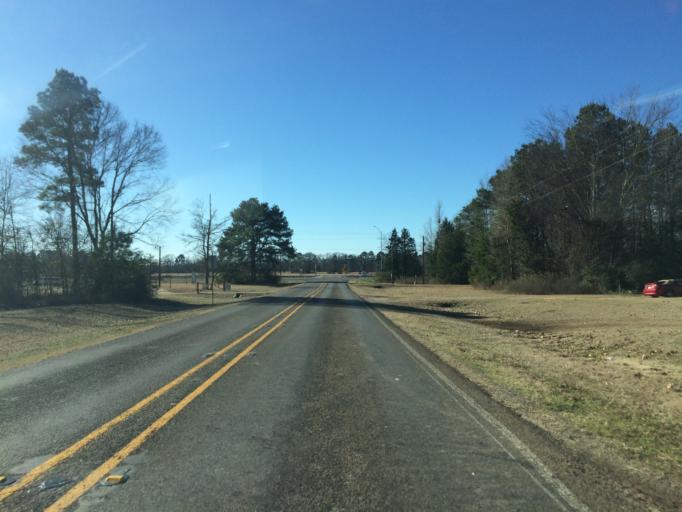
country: US
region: Texas
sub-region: Wood County
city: Hawkins
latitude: 32.6051
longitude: -95.2748
